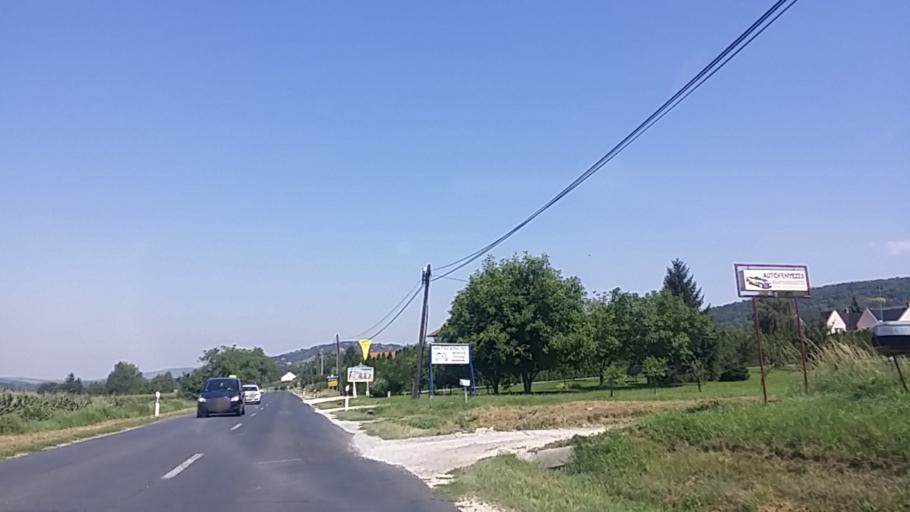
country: HU
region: Zala
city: Cserszegtomaj
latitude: 46.8043
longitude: 17.2066
